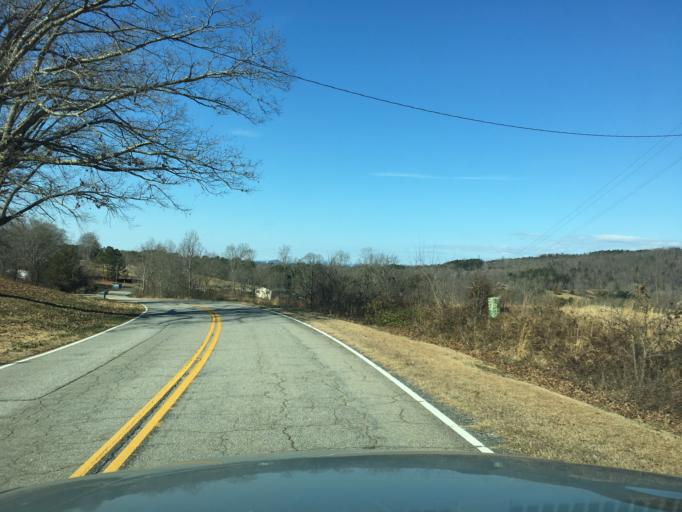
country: US
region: South Carolina
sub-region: Pickens County
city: Pickens
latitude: 34.8756
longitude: -82.6689
